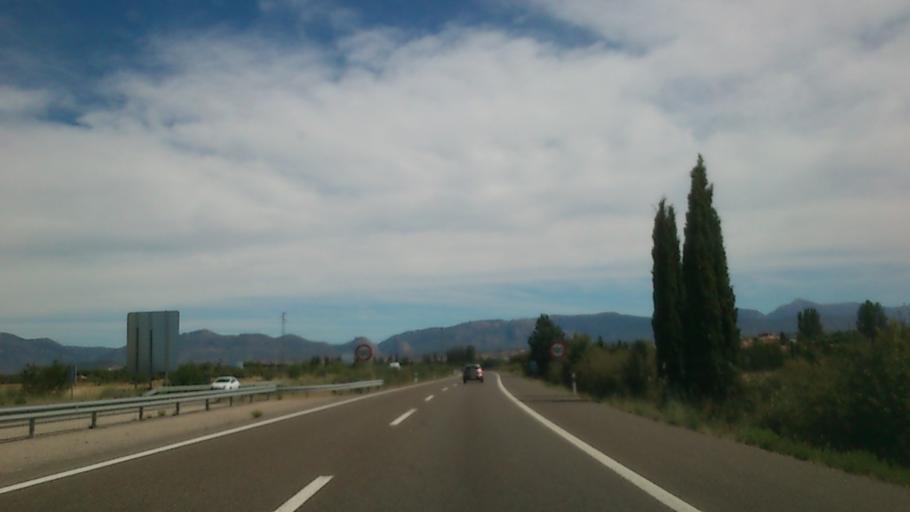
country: ES
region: Aragon
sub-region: Provincia de Huesca
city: Huesca
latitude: 42.1289
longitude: -0.4316
